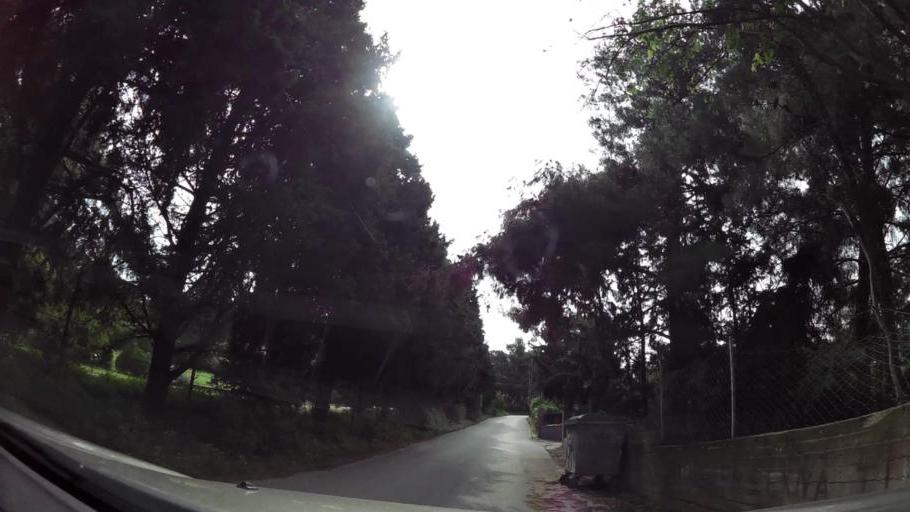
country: GR
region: Central Macedonia
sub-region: Nomos Thessalonikis
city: Panorama
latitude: 40.5905
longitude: 23.0129
